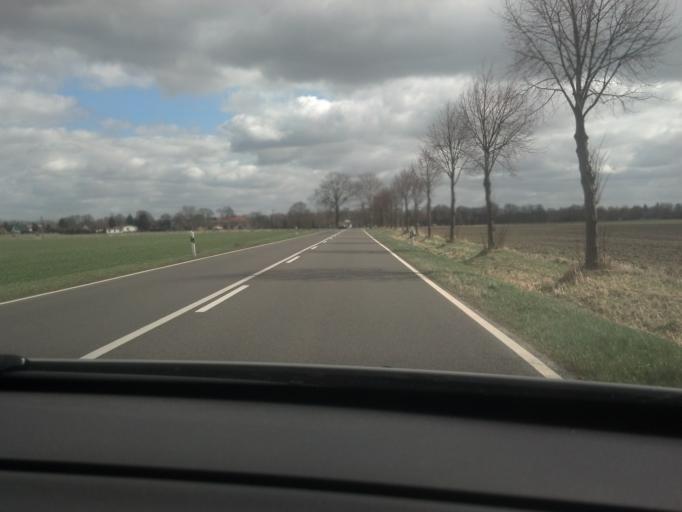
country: DE
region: Mecklenburg-Vorpommern
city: Rechlin
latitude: 53.3314
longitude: 12.6759
